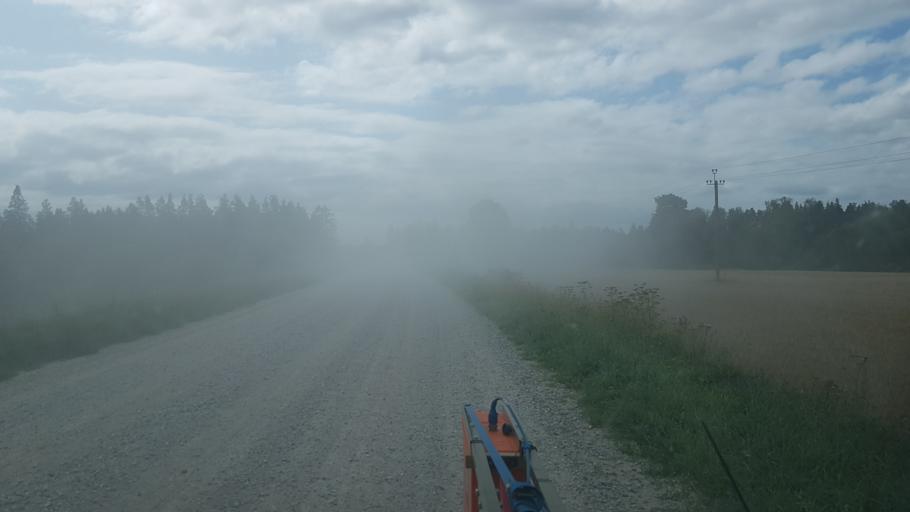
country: EE
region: Paernumaa
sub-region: Halinga vald
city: Parnu-Jaagupi
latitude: 58.5811
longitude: 24.4058
